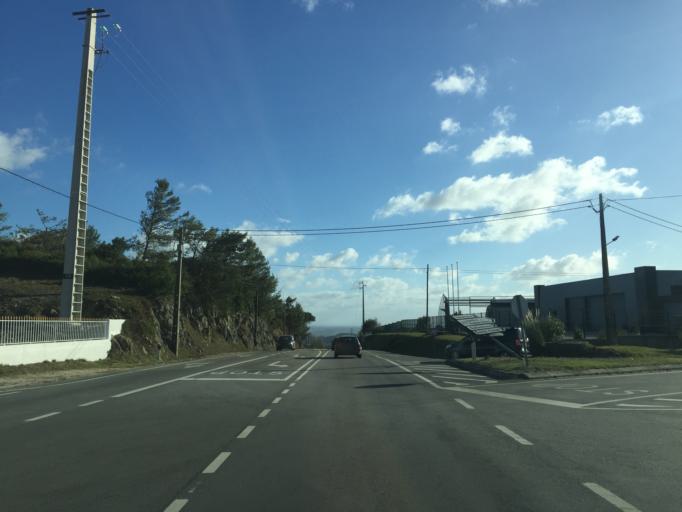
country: PT
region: Coimbra
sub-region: Figueira da Foz
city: Tavarede
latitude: 40.1900
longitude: -8.8303
